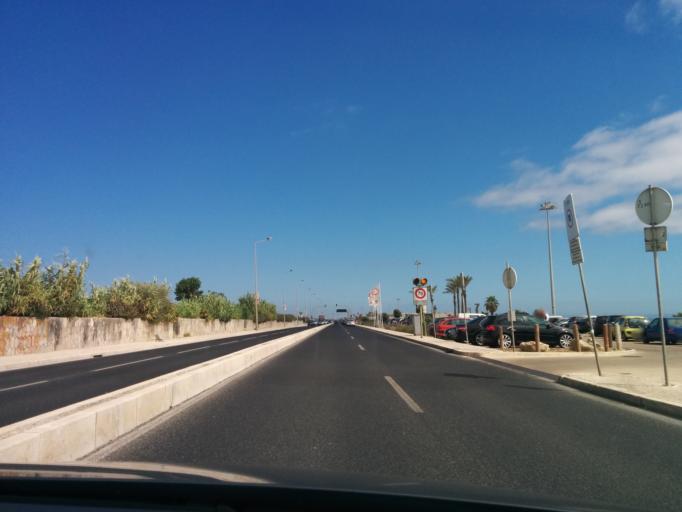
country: PT
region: Lisbon
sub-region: Oeiras
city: Carcavelos
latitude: 38.6804
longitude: -9.3350
